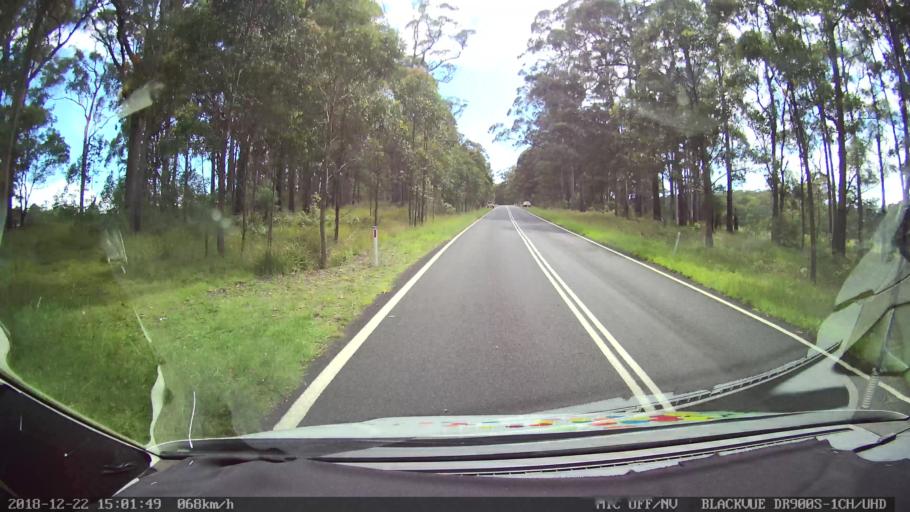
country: AU
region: New South Wales
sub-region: Bellingen
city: Dorrigo
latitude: -30.2581
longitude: 152.4564
